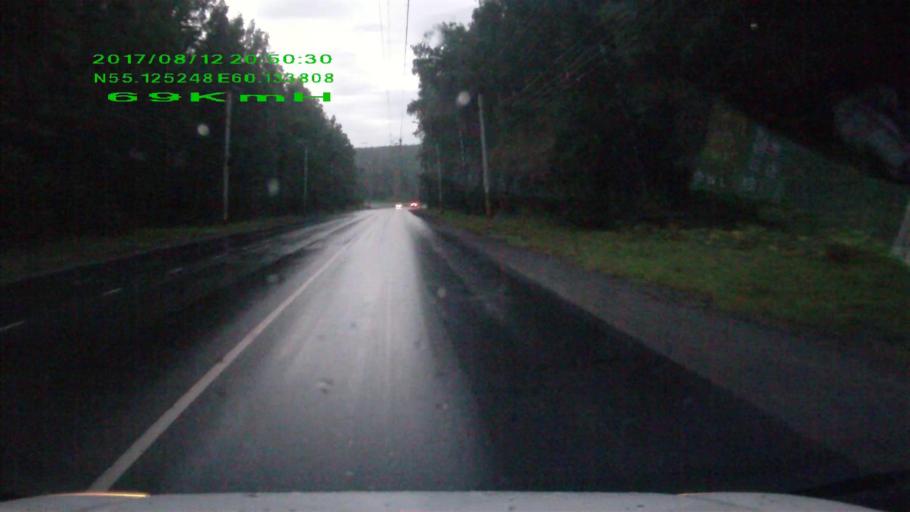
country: RU
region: Chelyabinsk
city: Turgoyak
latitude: 55.1254
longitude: 60.1339
